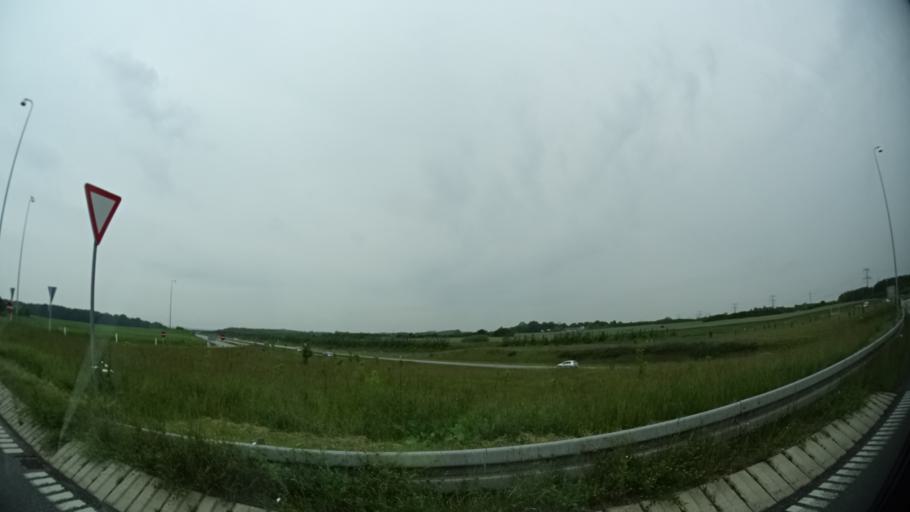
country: DK
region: Central Jutland
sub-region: Arhus Kommune
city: Logten
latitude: 56.2482
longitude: 10.3010
